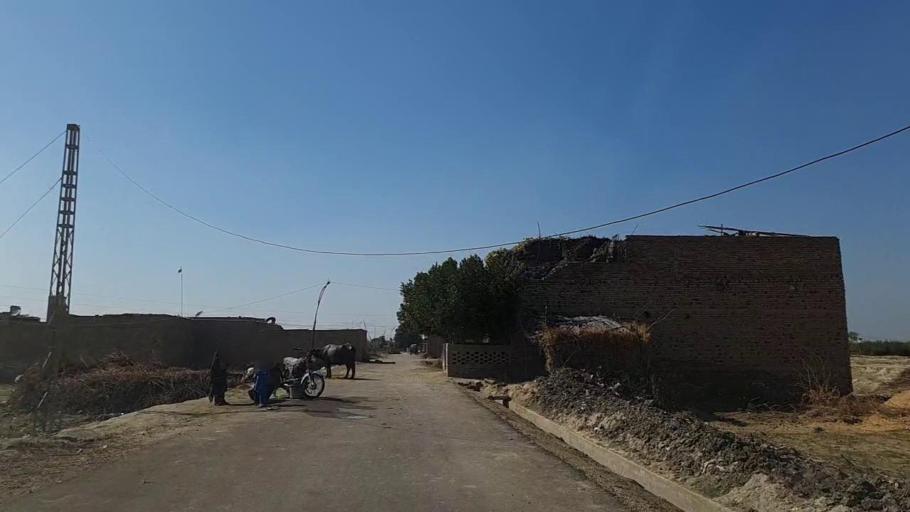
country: PK
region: Sindh
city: Nawabshah
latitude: 26.2547
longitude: 68.4382
